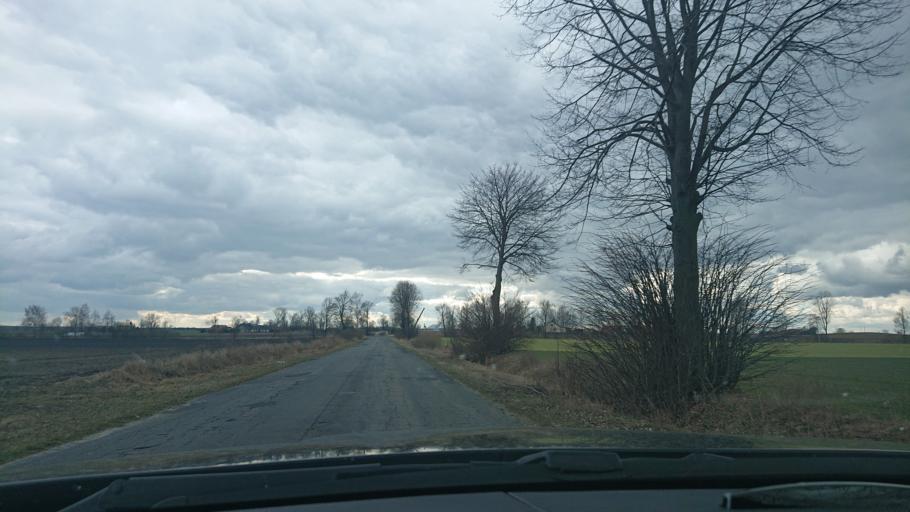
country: PL
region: Greater Poland Voivodeship
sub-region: Powiat gnieznienski
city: Niechanowo
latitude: 52.5868
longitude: 17.6948
